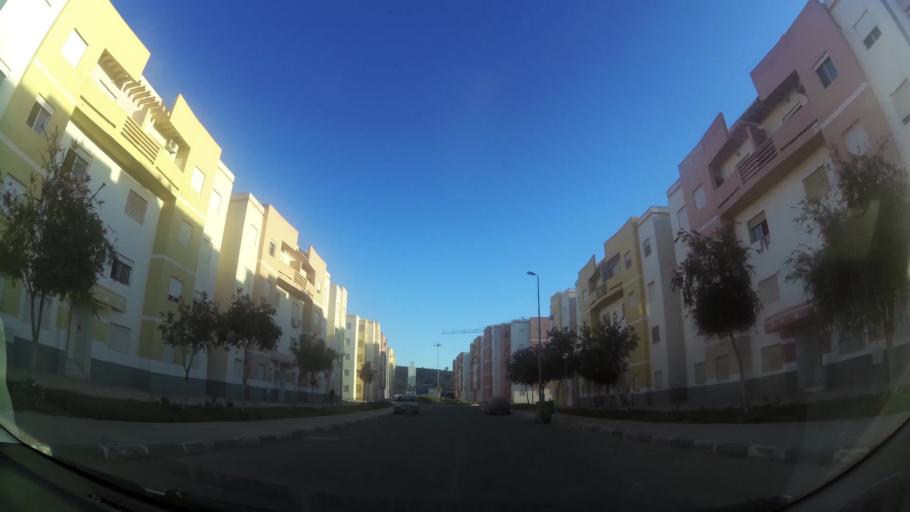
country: MA
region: Oriental
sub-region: Berkane-Taourirt
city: Madagh
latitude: 35.0774
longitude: -2.2375
